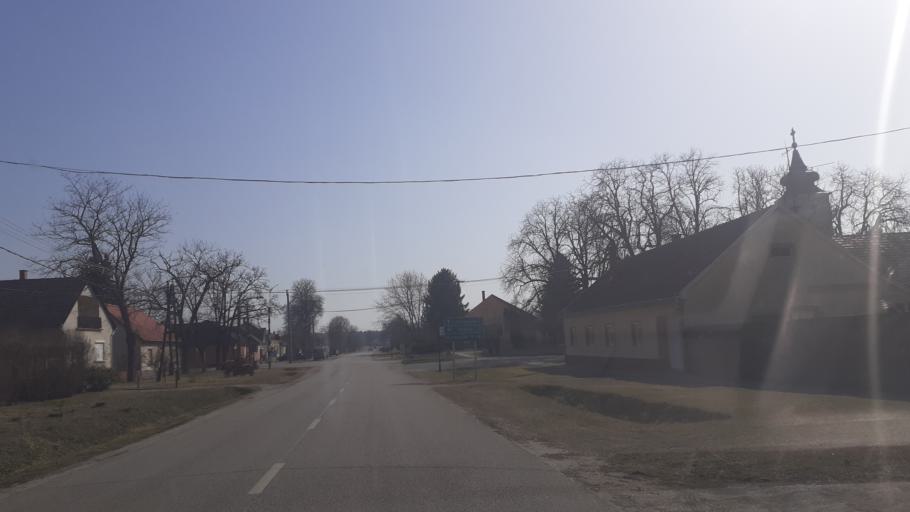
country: HU
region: Pest
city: Orkeny
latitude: 47.0820
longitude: 19.3690
